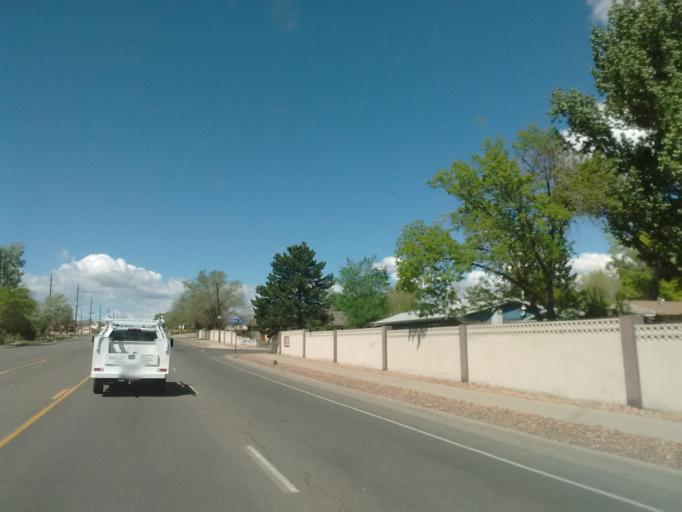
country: US
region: Colorado
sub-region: Mesa County
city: Fruitvale
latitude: 39.0919
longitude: -108.5183
